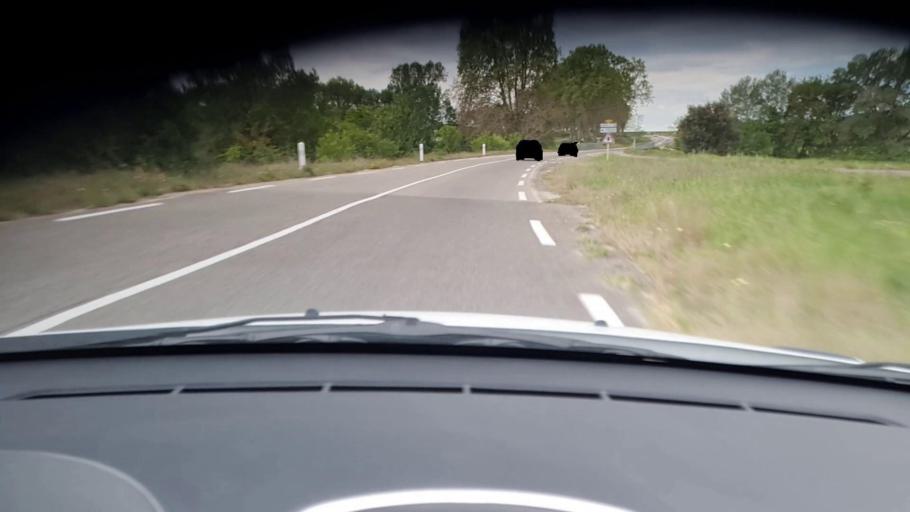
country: FR
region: Languedoc-Roussillon
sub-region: Departement du Gard
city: Uzes
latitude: 43.9837
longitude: 4.4141
